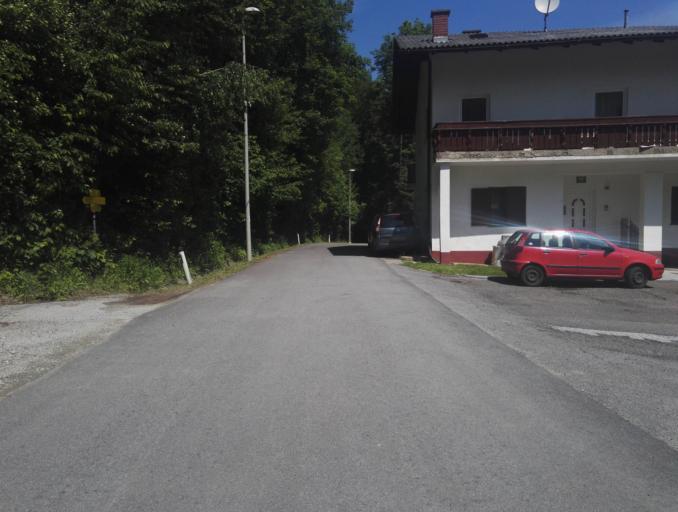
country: AT
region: Styria
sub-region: Graz Stadt
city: Goesting
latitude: 47.1086
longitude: 15.3727
